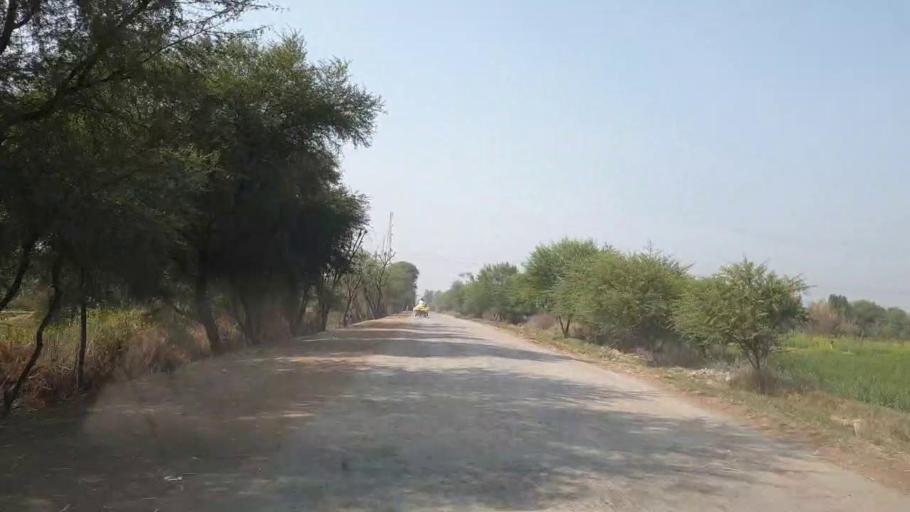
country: PK
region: Sindh
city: Mirpur Khas
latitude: 25.7063
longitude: 69.1329
